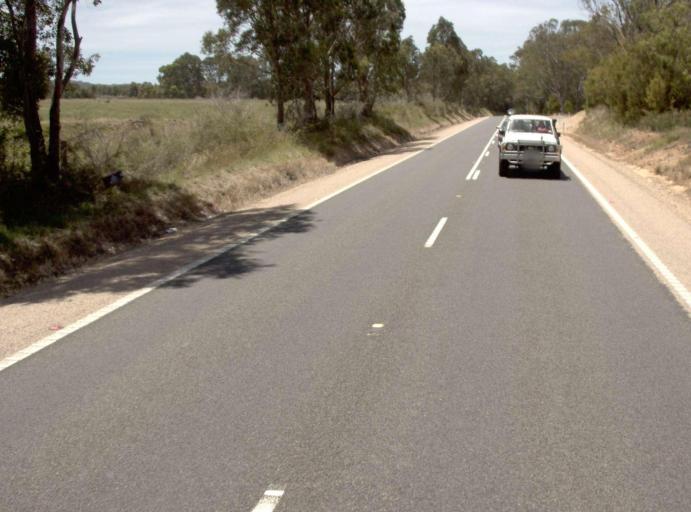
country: AU
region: Victoria
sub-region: East Gippsland
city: Bairnsdale
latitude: -37.7554
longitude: 147.7126
